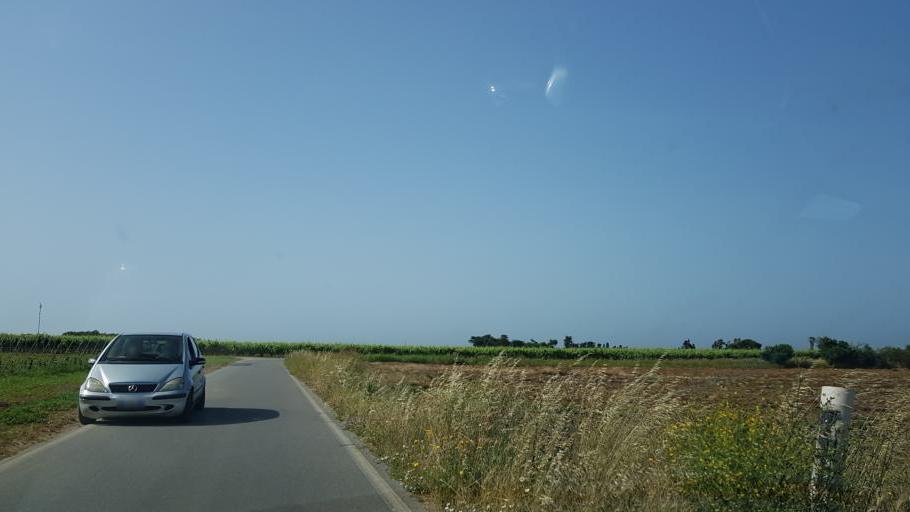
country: IT
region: Apulia
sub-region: Provincia di Brindisi
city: Brindisi
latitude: 40.6755
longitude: 17.8863
